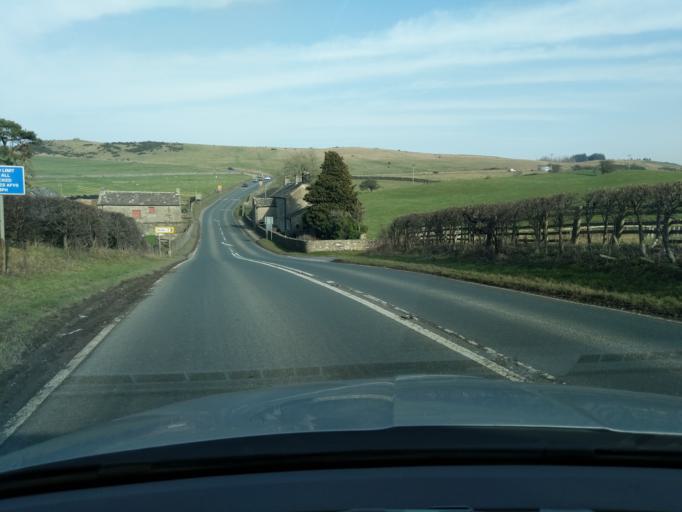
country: GB
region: England
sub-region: North Yorkshire
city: Leyburn
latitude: 54.3500
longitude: -1.8072
